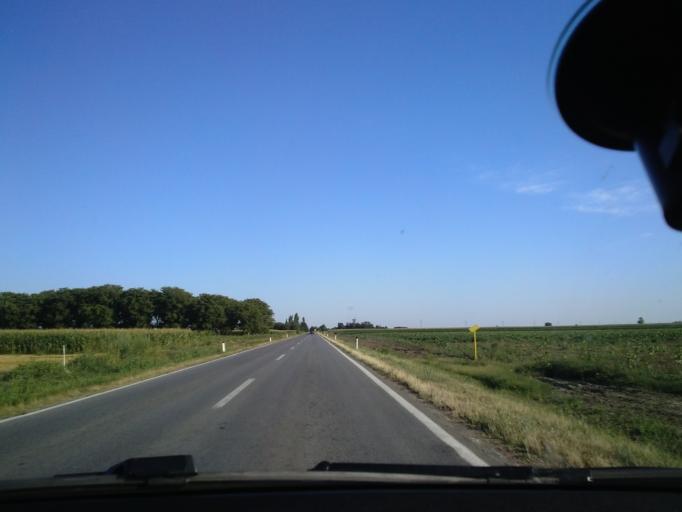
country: RS
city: Prigrevica
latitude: 45.6926
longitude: 19.1719
